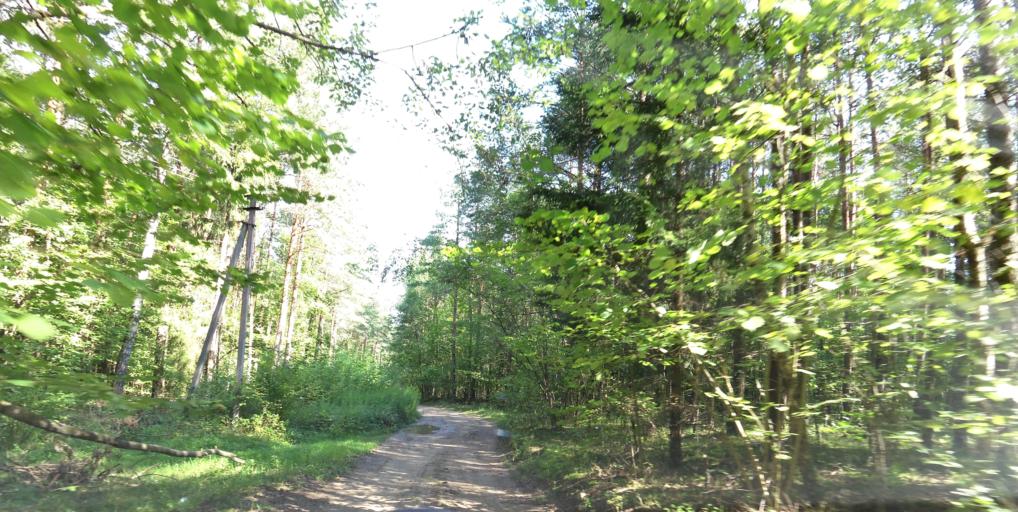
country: LT
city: Grigiskes
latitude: 54.7439
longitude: 25.0227
